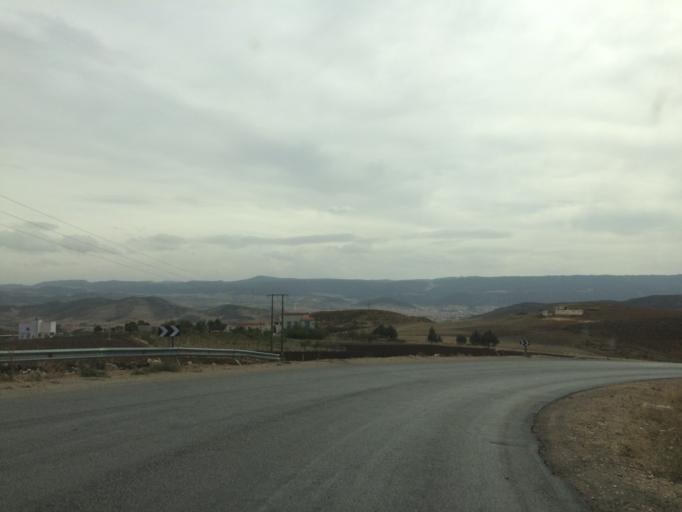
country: MA
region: Meknes-Tafilalet
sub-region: Ifrane
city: Azrou
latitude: 33.4979
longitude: -5.2606
